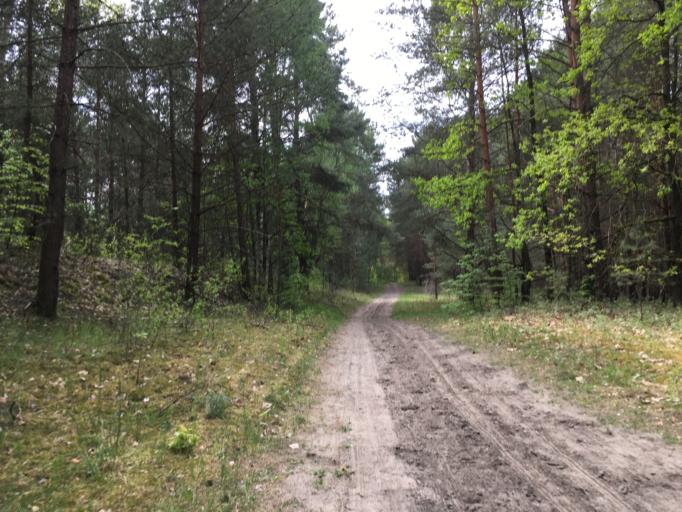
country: DE
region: Brandenburg
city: Rudnitz
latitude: 52.7053
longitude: 13.6226
